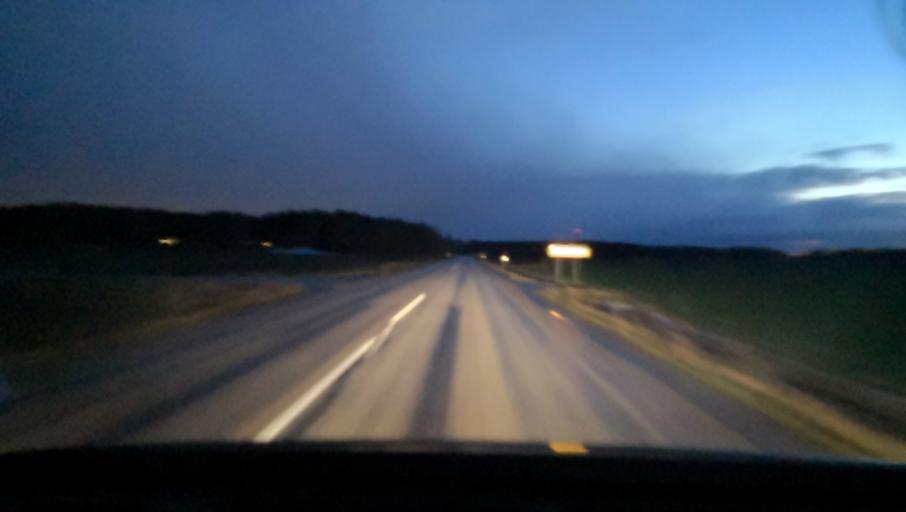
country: SE
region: Vaestmanland
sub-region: Vasteras
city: Skultuna
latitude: 59.7507
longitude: 16.4550
